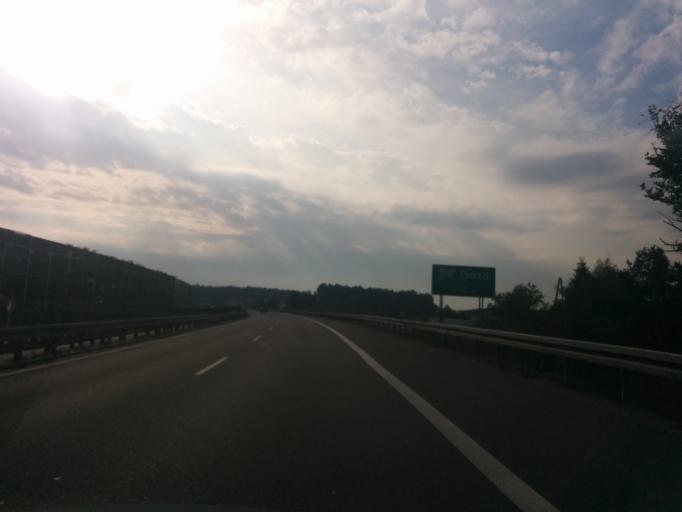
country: PL
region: Masovian Voivodeship
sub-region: Powiat bialobrzeski
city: Stara Blotnica
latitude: 51.5806
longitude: 21.0022
